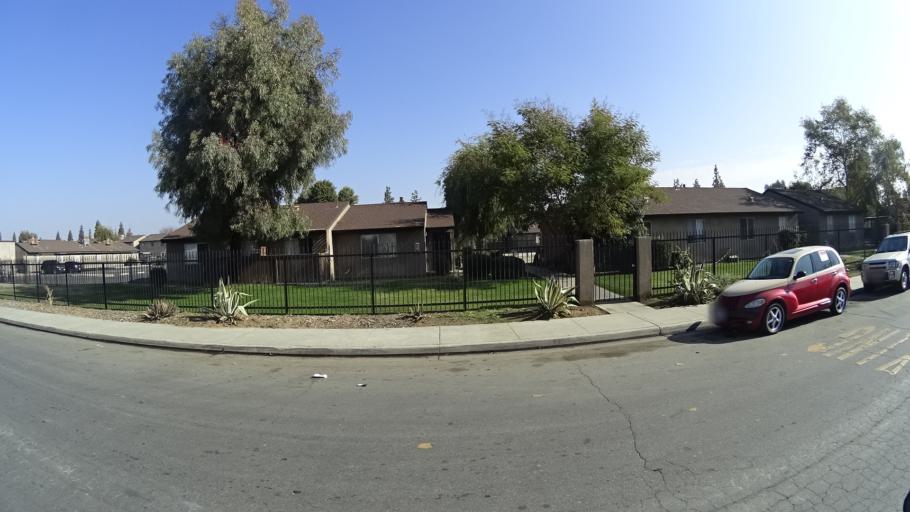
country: US
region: California
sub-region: Kern County
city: Bakersfield
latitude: 35.3950
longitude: -119.0129
